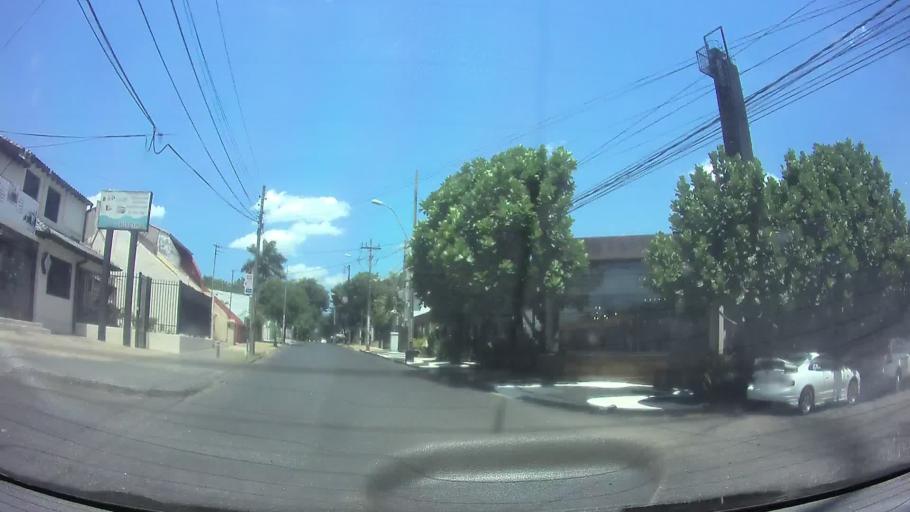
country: PY
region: Asuncion
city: Asuncion
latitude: -25.2961
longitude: -57.5891
